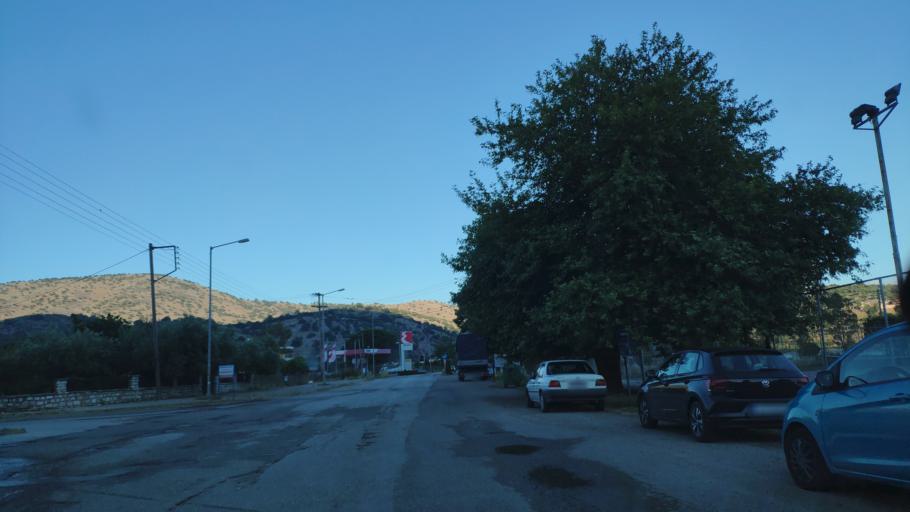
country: GR
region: West Greece
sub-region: Nomos Aitolias kai Akarnanias
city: Astakos
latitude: 38.5353
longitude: 21.0890
